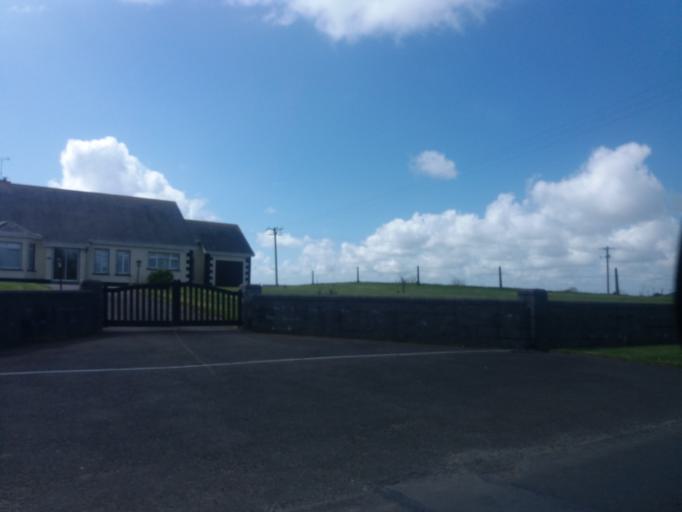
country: IE
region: Leinster
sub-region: Loch Garman
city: Castlebridge
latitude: 52.3892
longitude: -6.3752
